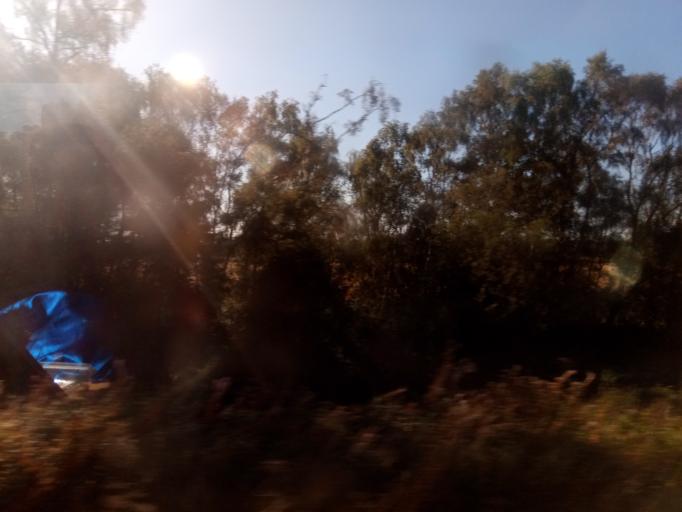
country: GB
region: England
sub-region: Cambridgeshire
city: Yaxley
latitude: 52.4854
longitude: -0.2374
